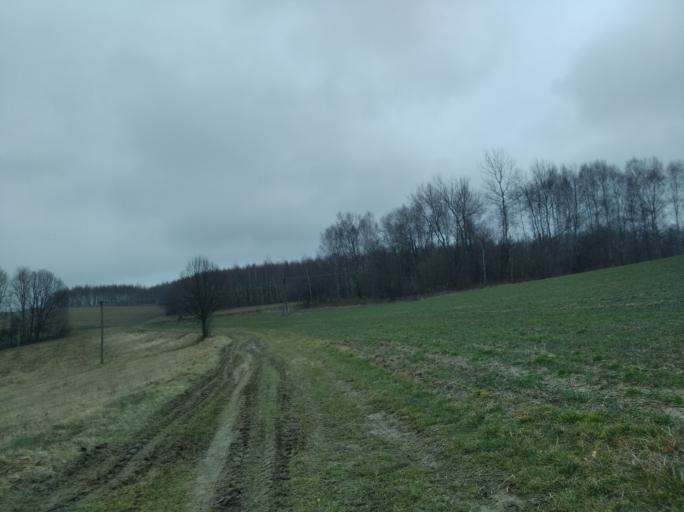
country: PL
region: Subcarpathian Voivodeship
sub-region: Powiat strzyzowski
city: Strzyzow
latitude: 49.9062
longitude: 21.7883
